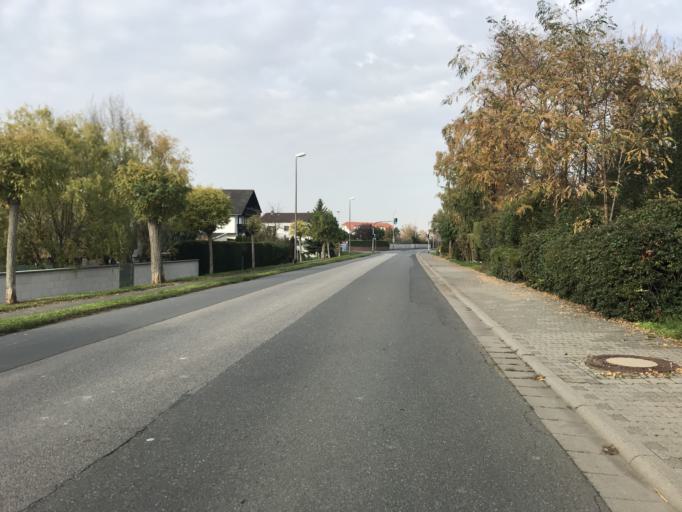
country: DE
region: Hesse
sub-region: Regierungsbezirk Darmstadt
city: Trebur
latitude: 49.9364
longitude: 8.3809
